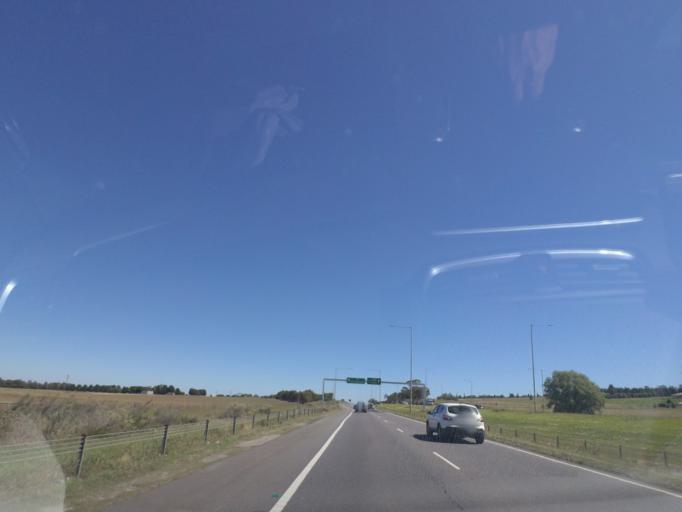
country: AU
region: Victoria
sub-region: Hume
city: Craigieburn
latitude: -37.5651
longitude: 144.9417
